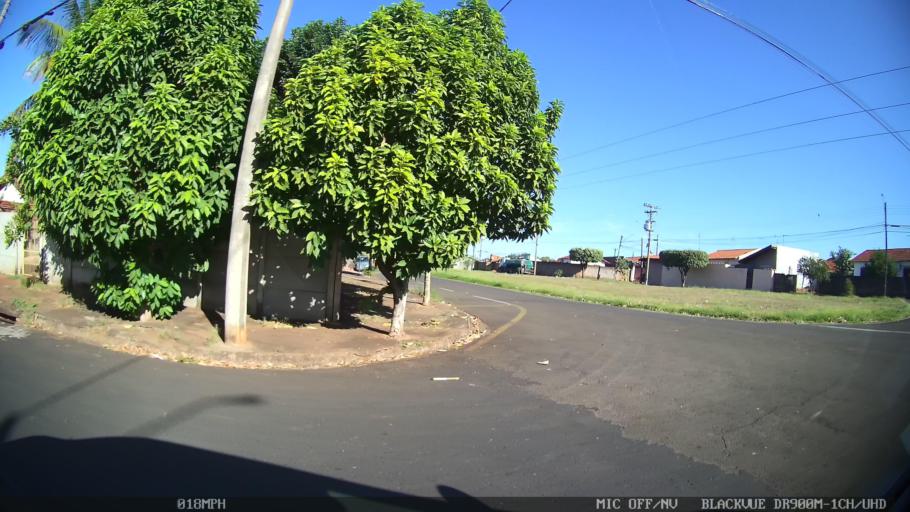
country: BR
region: Sao Paulo
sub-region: Olimpia
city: Olimpia
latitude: -20.7423
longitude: -48.8885
